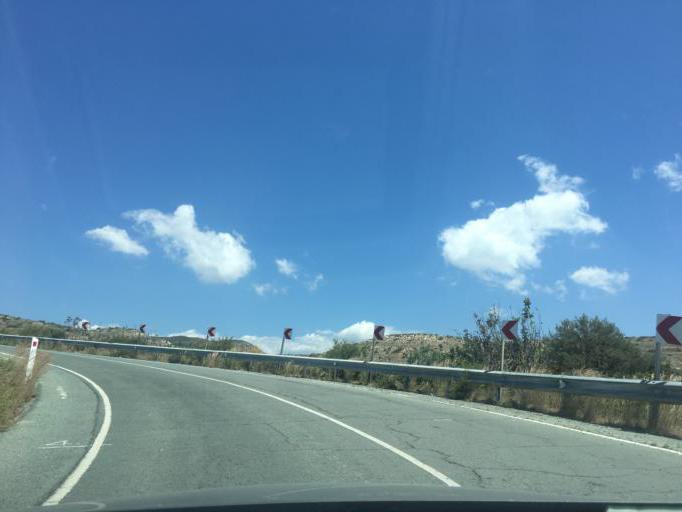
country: CY
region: Limassol
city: Mouttagiaka
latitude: 34.7429
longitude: 33.0645
